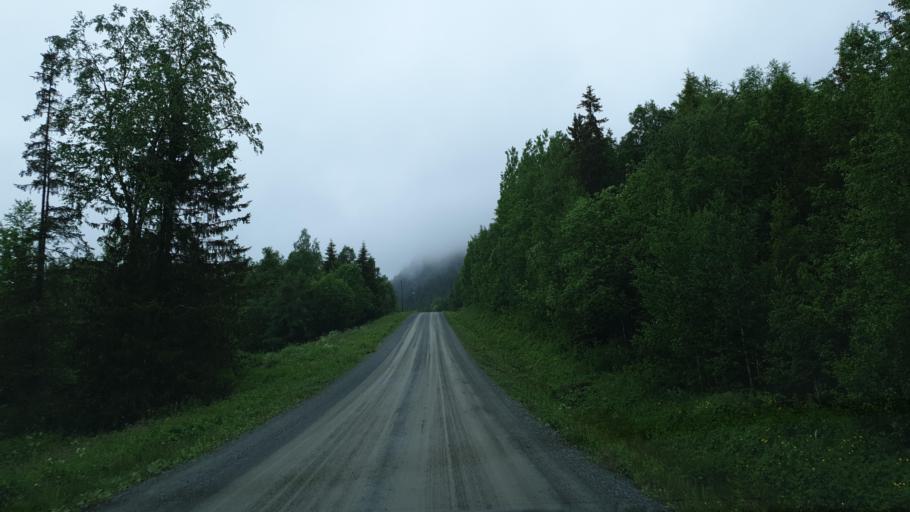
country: SE
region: Vaesterbotten
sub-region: Vilhelmina Kommun
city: Sjoberg
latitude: 65.3439
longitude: 15.8680
